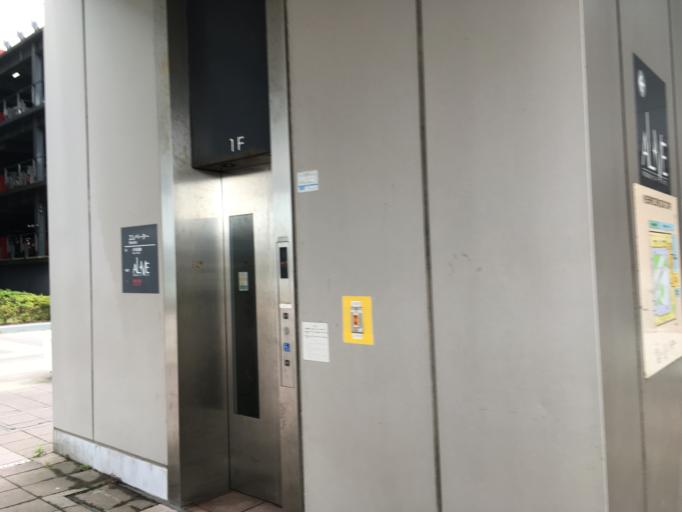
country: JP
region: Akita
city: Akita
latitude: 39.7165
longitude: 140.1310
